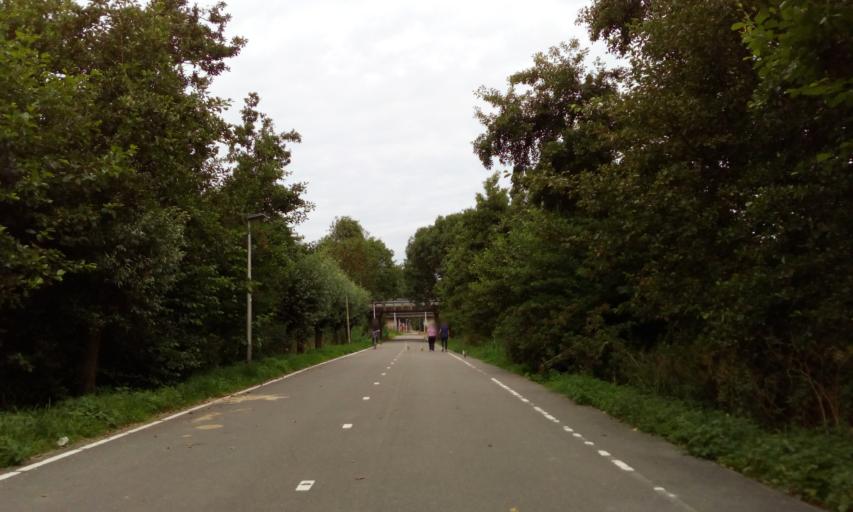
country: NL
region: South Holland
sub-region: Gemeente Capelle aan den IJssel
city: Capelle aan den IJssel
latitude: 51.9539
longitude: 4.5917
